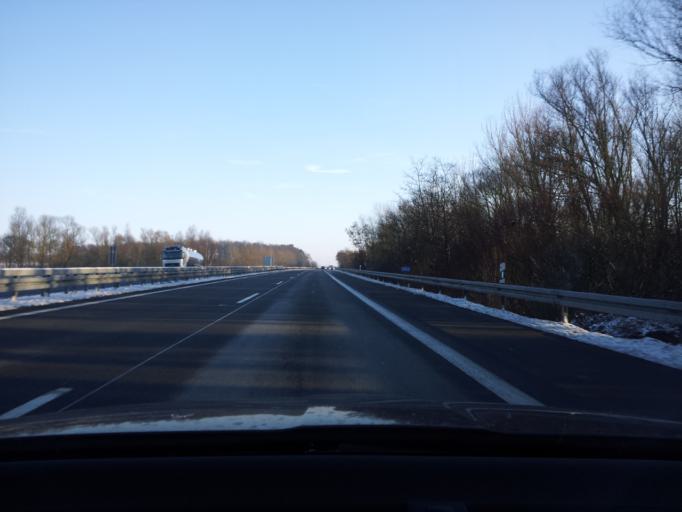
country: DE
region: Brandenburg
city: Gerdshagen
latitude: 53.2283
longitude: 12.2172
